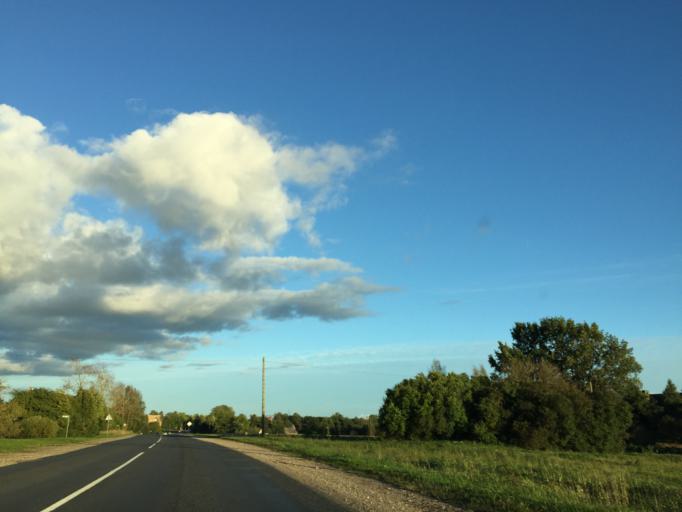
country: LV
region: Saldus Rajons
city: Saldus
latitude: 56.6955
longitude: 22.4375
